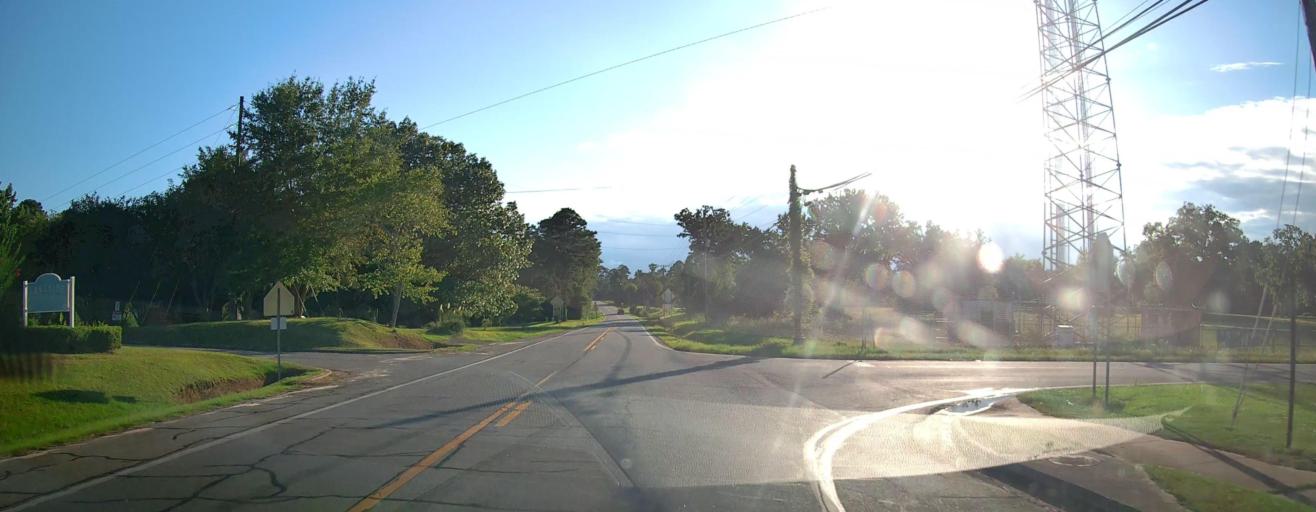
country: US
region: Georgia
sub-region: Pulaski County
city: Hawkinsville
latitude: 32.2789
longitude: -83.4919
